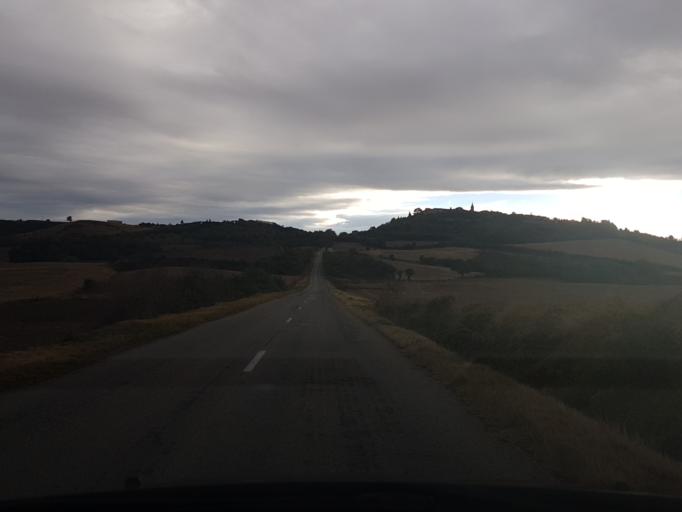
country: FR
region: Languedoc-Roussillon
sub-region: Departement de l'Aude
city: Bram
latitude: 43.1900
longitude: 2.0485
